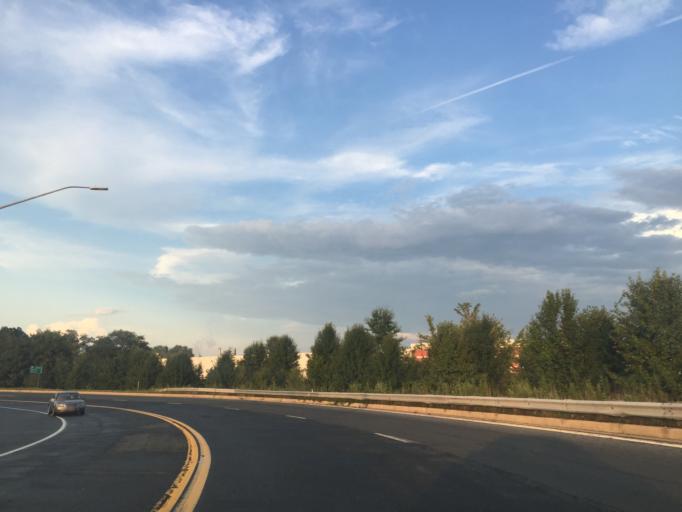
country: US
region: Maryland
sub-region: Harford County
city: Riverside
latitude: 39.4698
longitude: -76.2329
